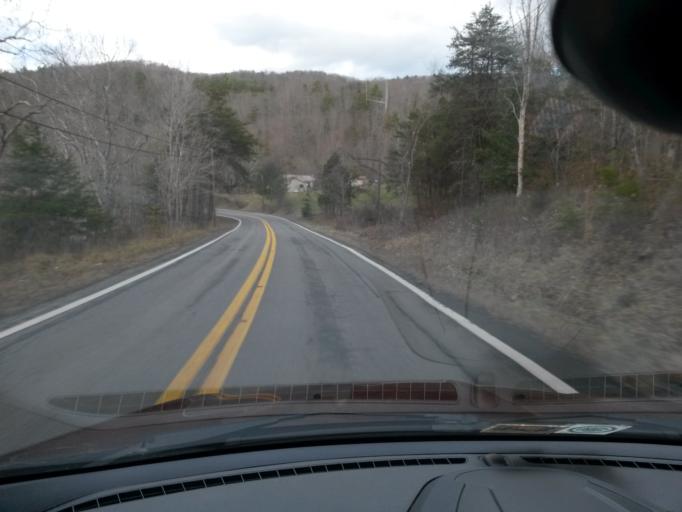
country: US
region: West Virginia
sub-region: Monroe County
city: Union
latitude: 37.5070
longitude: -80.6094
